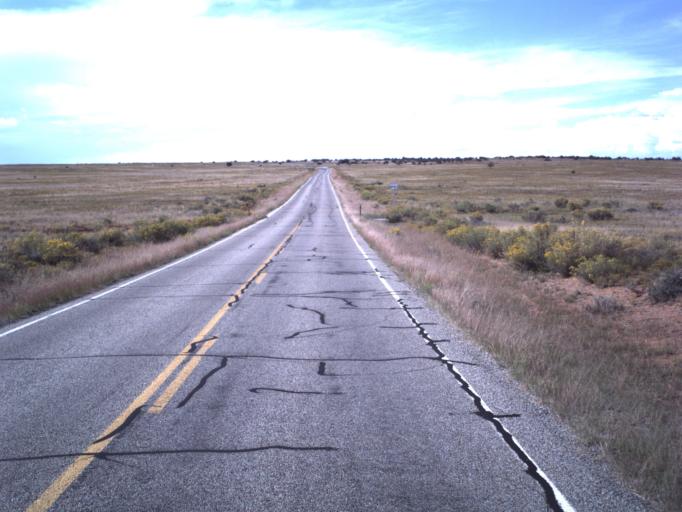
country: US
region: Utah
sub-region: Grand County
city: Moab
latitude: 38.5380
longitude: -109.7560
